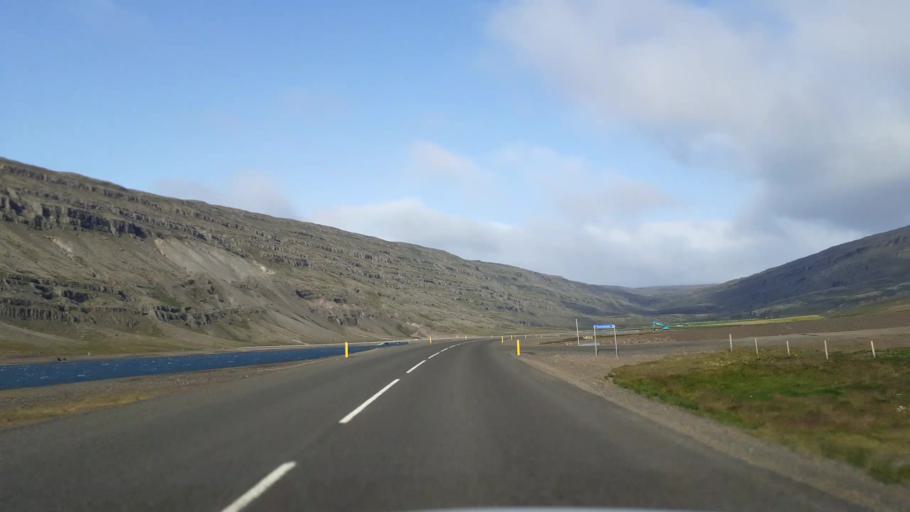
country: IS
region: East
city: Reydarfjoerdur
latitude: 64.7885
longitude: -14.4660
